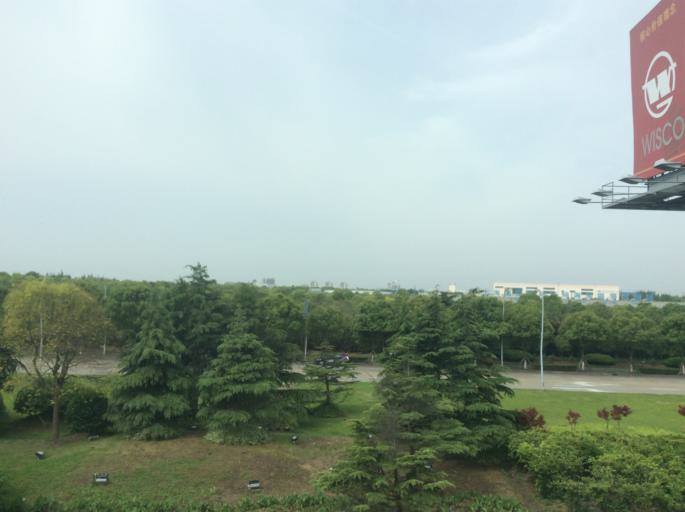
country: CN
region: Shanghai Shi
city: Laogang
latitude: 31.1768
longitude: 121.7874
